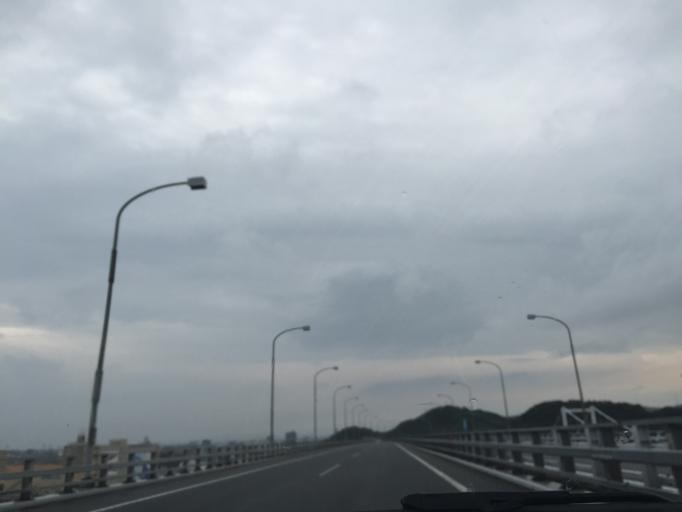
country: JP
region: Tokushima
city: Narutocho-mitsuishi
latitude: 34.1929
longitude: 134.6131
